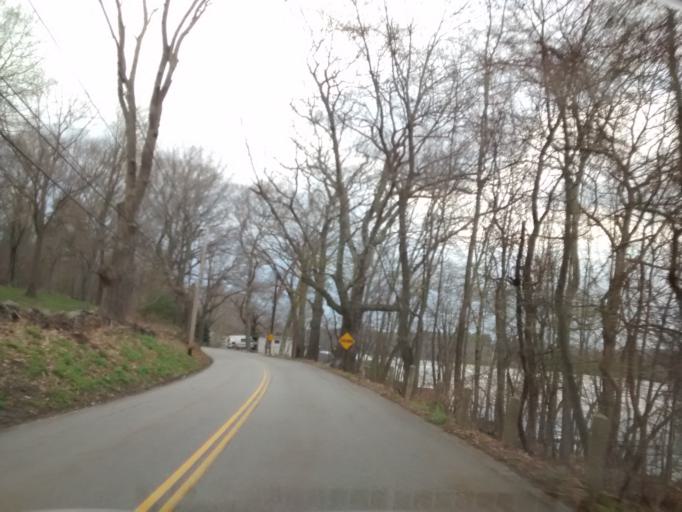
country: US
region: Massachusetts
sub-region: Worcester County
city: Sutton
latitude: 42.1585
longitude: -71.7856
